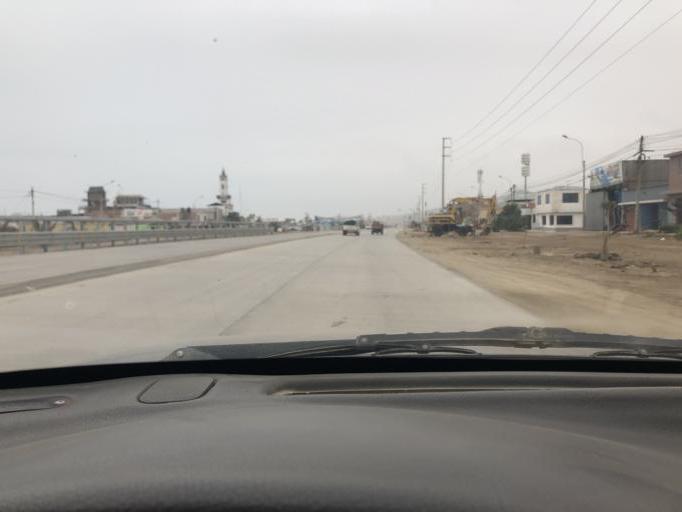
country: PE
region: Lima
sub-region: Lima
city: San Bartolo
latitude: -12.3686
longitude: -76.7917
